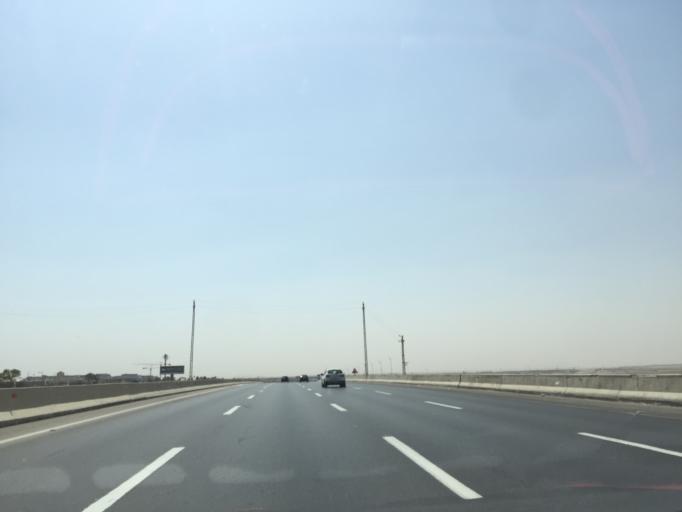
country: EG
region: Al Jizah
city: Awsim
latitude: 30.0805
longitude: 30.9534
